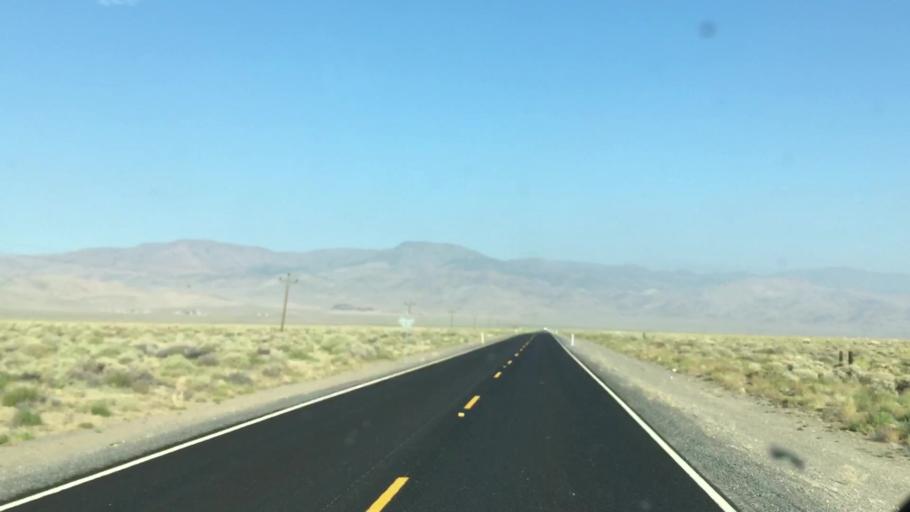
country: US
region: Nevada
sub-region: Lyon County
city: Fernley
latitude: 39.6441
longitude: -119.3072
